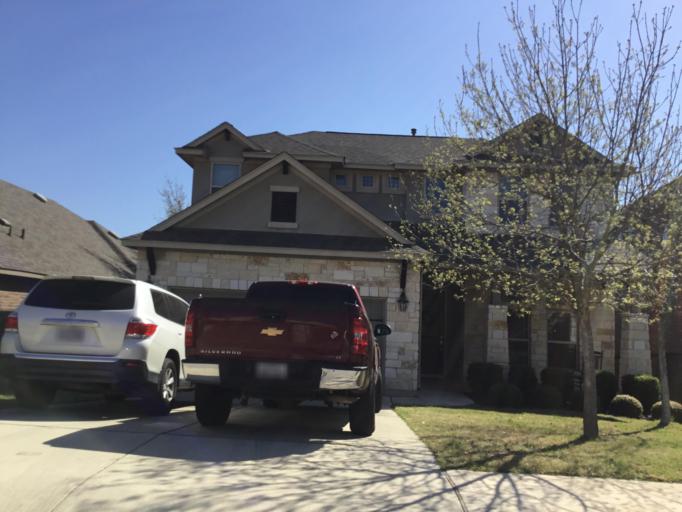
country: US
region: Texas
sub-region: Williamson County
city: Brushy Creek
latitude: 30.5735
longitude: -97.7676
